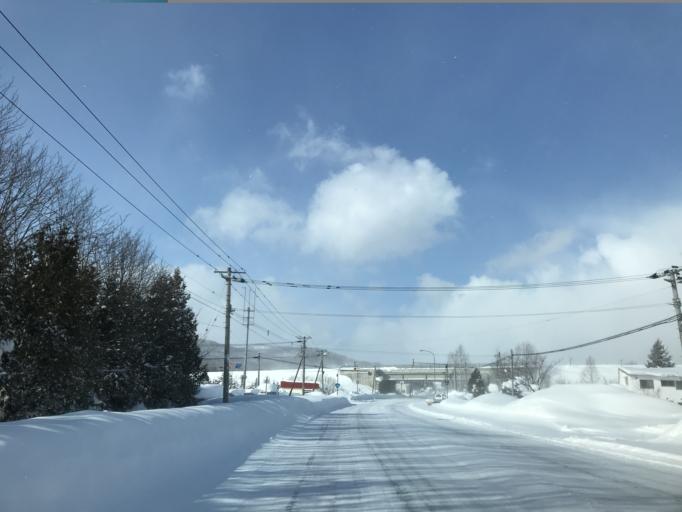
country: JP
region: Hokkaido
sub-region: Asahikawa-shi
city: Asahikawa
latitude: 43.9213
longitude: 142.4790
